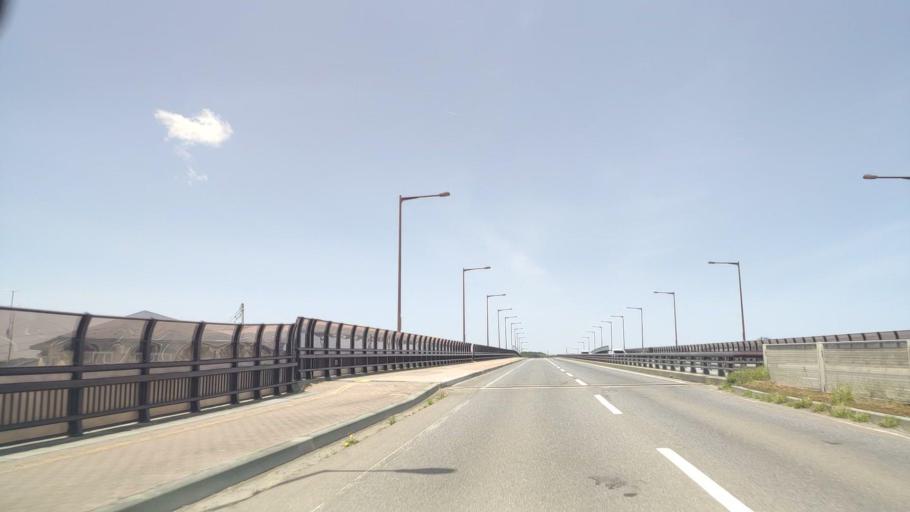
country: JP
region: Aomori
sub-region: Hachinohe Shi
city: Uchimaru
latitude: 40.5129
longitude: 141.4383
